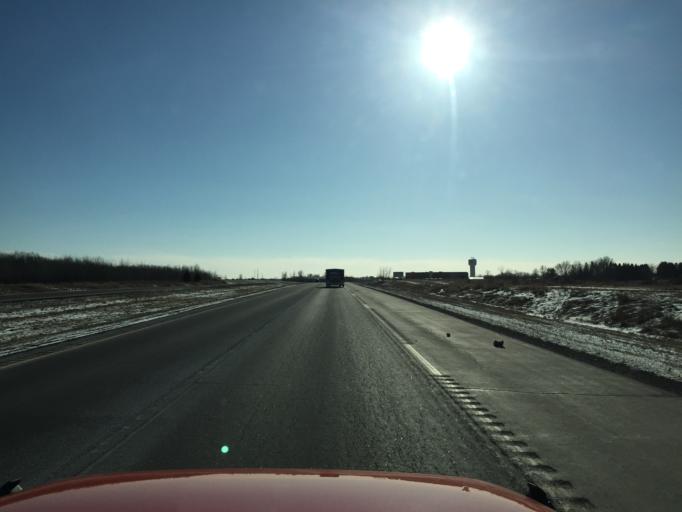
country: US
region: Minnesota
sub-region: Mille Lacs County
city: Milaca
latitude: 45.7718
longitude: -93.6460
